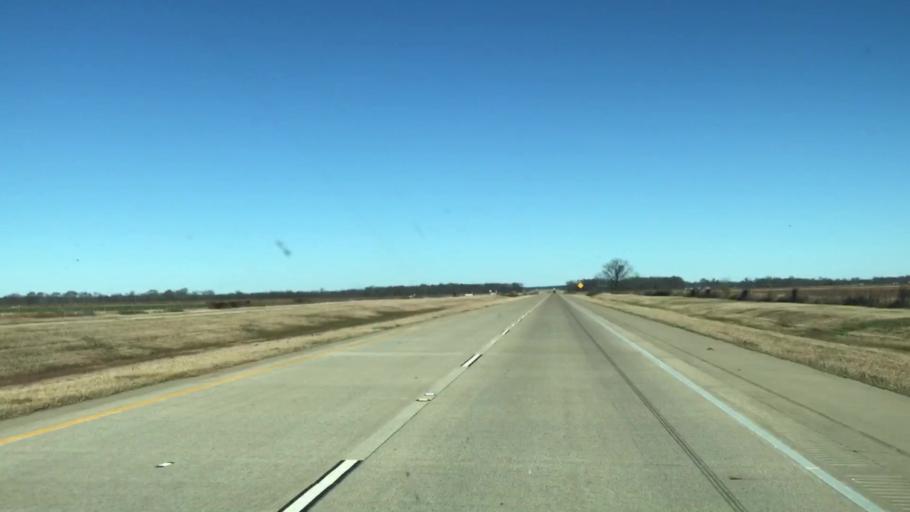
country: US
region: Louisiana
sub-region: Caddo Parish
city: Oil City
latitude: 32.7274
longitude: -93.8719
